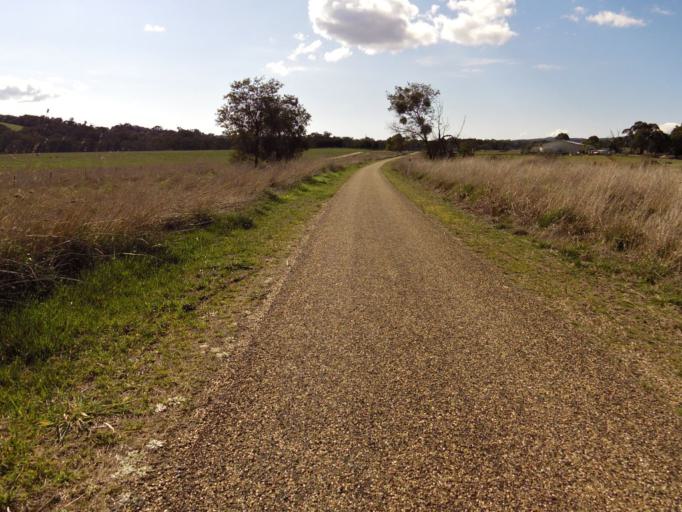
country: AU
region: Victoria
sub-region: Wangaratta
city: Wangaratta
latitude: -36.3963
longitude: 146.6540
